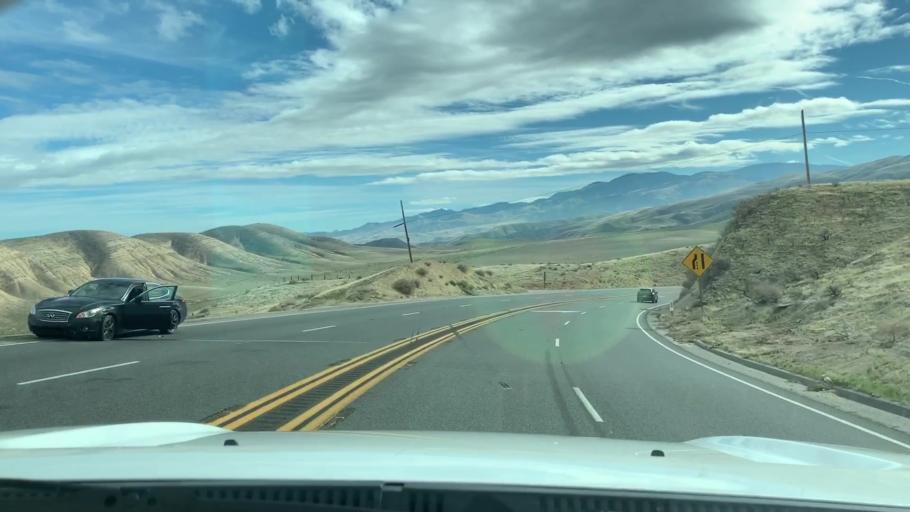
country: US
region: California
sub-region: Kern County
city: Maricopa
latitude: 35.0043
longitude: -119.4171
